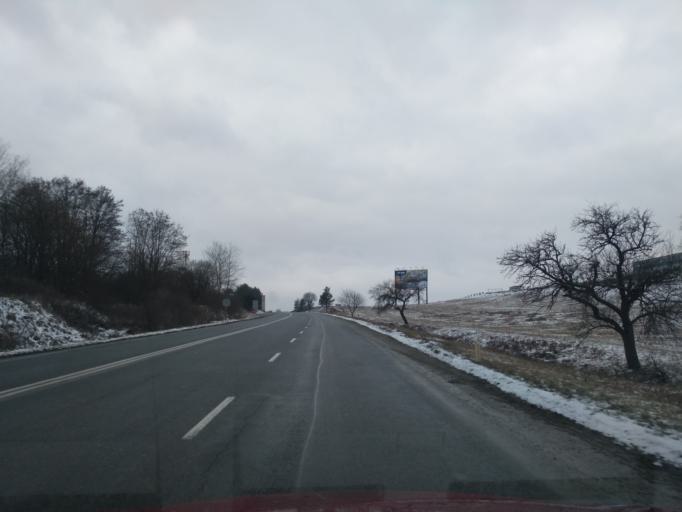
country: SK
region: Presovsky
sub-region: Okres Presov
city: Presov
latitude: 48.9992
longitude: 21.1992
